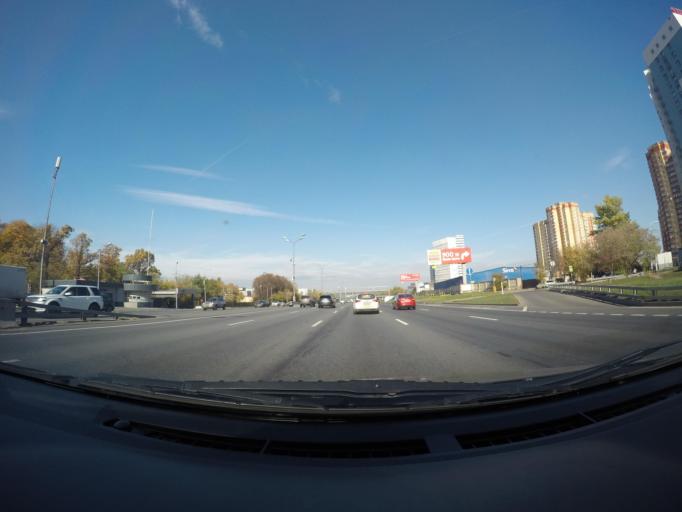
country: RU
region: Moscow
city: Vostochnyy
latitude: 55.8041
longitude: 37.8400
